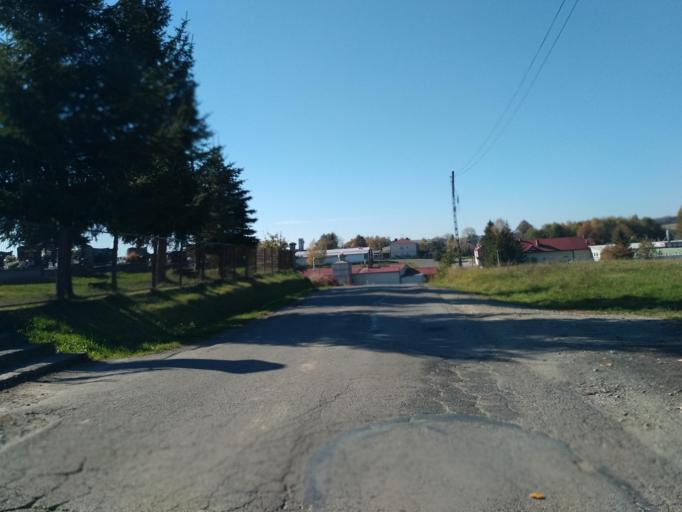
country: PL
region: Subcarpathian Voivodeship
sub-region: Powiat ropczycko-sedziszowski
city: Iwierzyce
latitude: 50.0232
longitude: 21.7686
